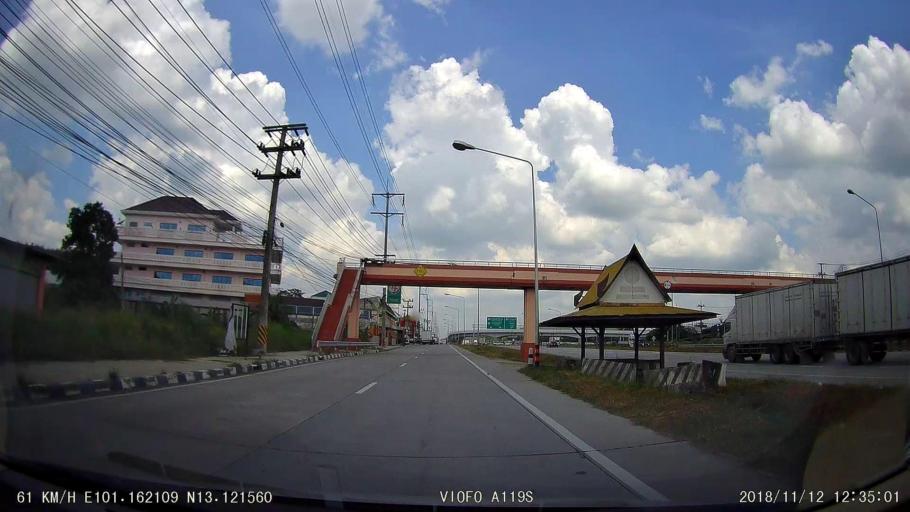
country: TH
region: Rayong
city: Pluak Daeng
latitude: 13.1218
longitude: 101.1622
